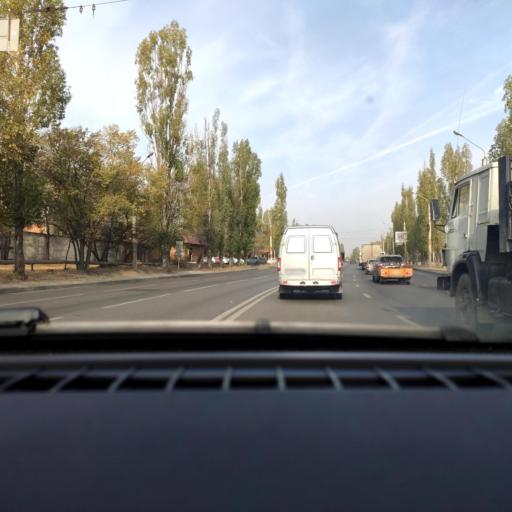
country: RU
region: Voronezj
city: Voronezh
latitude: 51.6242
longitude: 39.2330
